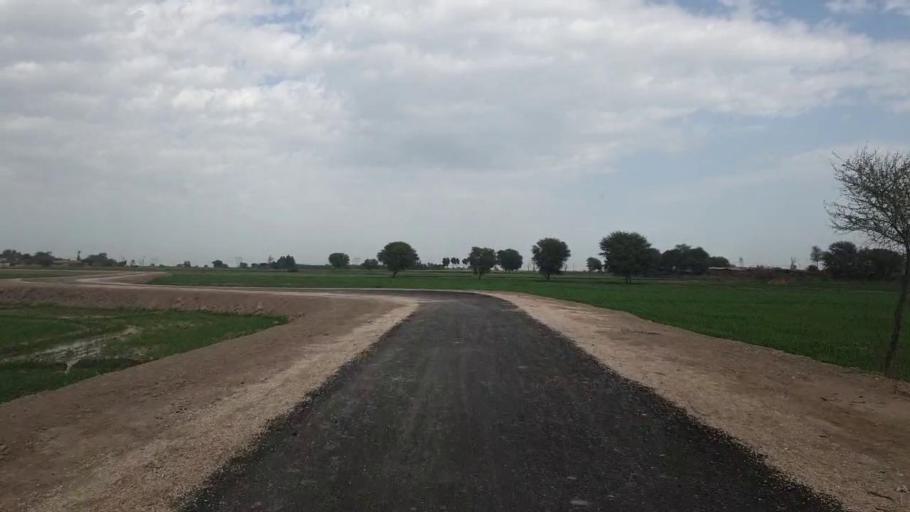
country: PK
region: Sindh
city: Hala
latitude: 25.9753
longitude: 68.3995
